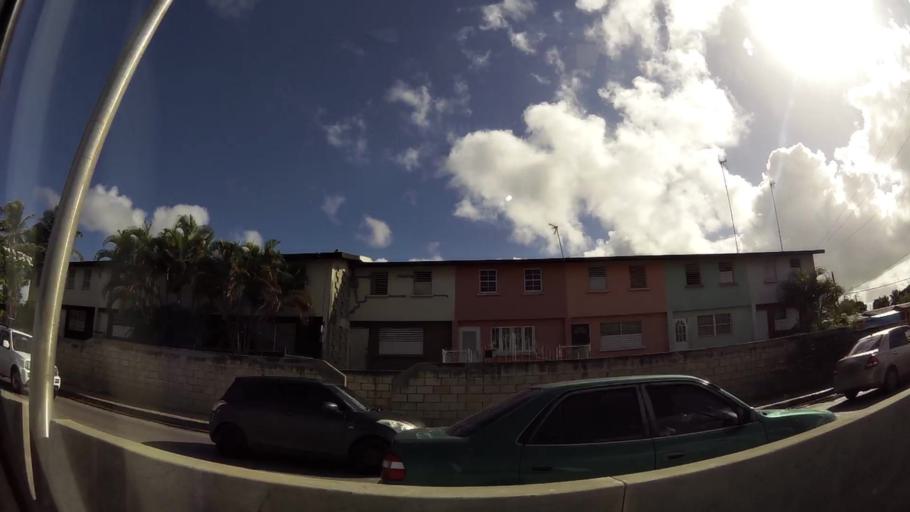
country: BB
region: Saint James
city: Holetown
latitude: 13.1590
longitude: -59.6147
